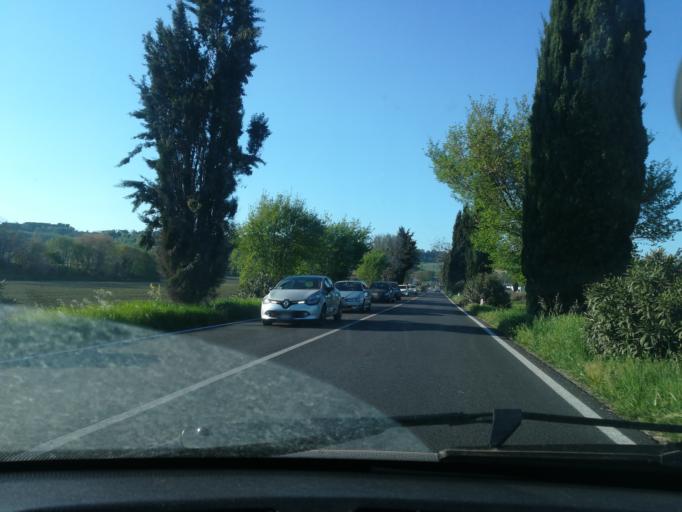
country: IT
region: The Marches
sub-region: Provincia di Macerata
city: Piediripa
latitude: 43.2775
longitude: 13.4857
